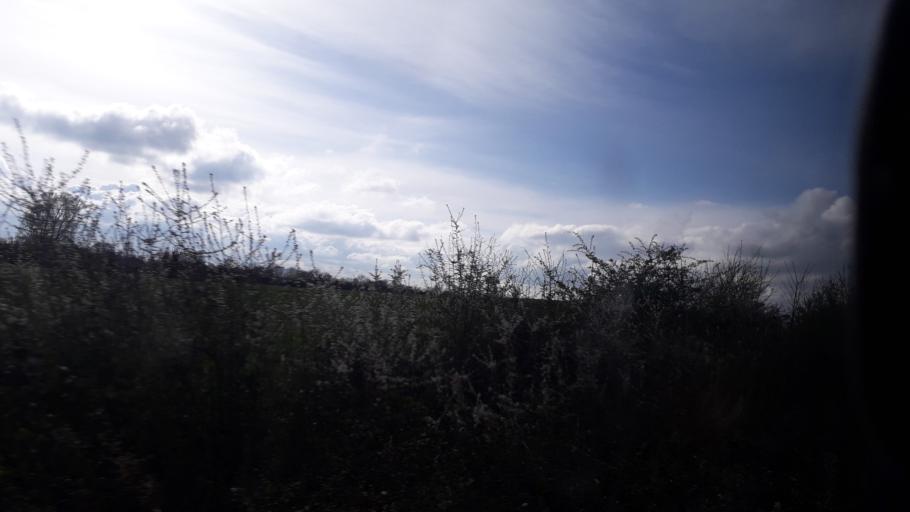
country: IE
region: Leinster
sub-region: An Mhi
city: Longwood
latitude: 53.4620
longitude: -6.9676
